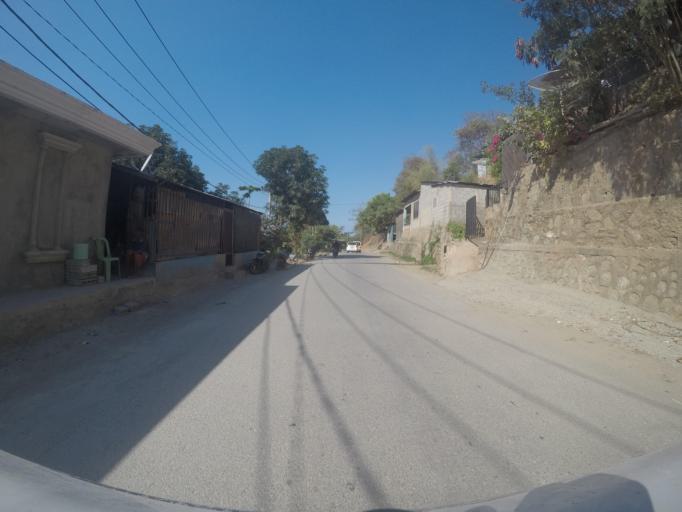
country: TL
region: Dili
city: Dili
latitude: -8.5698
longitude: 125.5436
